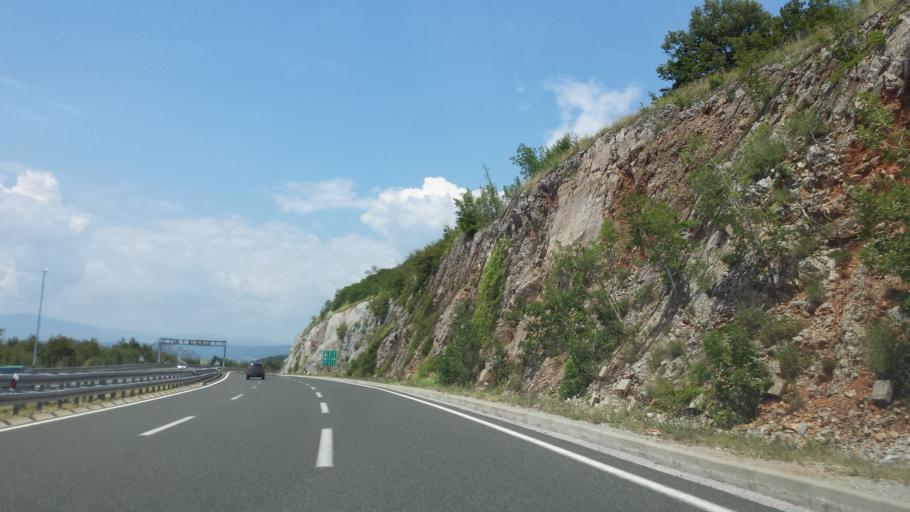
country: HR
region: Primorsko-Goranska
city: Krasica
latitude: 45.3494
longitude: 14.5896
